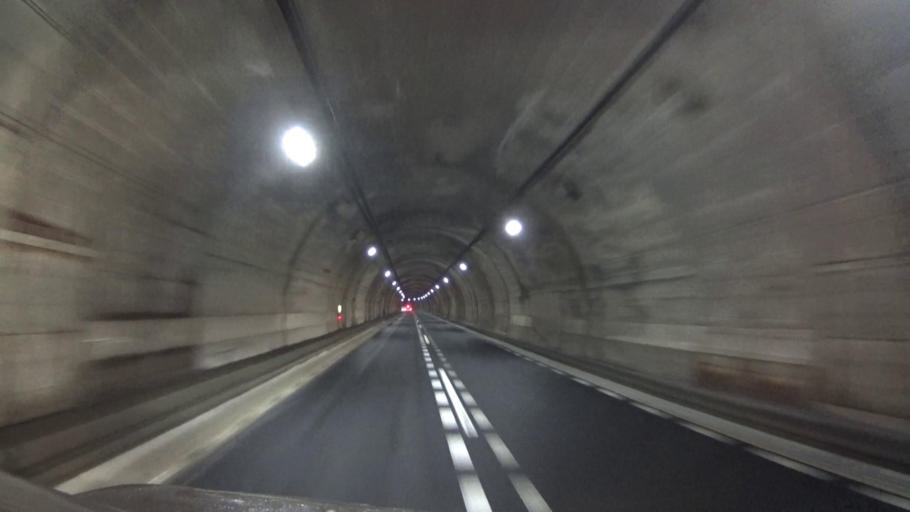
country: JP
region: Hokkaido
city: Otaru
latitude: 43.1647
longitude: 141.0948
